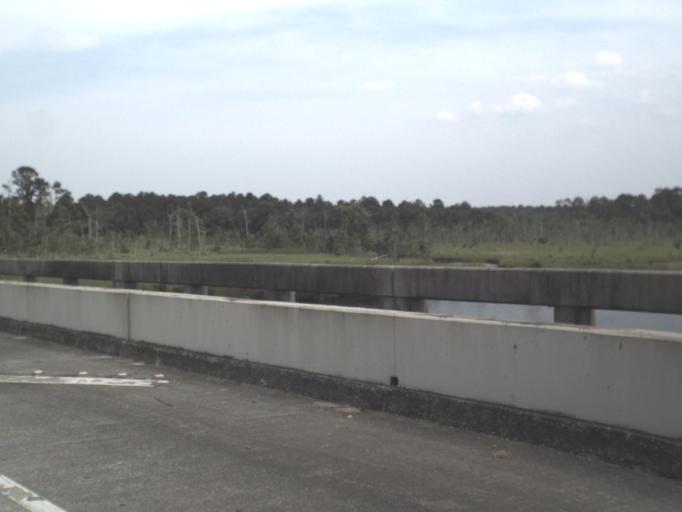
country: US
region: Florida
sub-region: Clay County
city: Bellair-Meadowbrook Terrace
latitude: 30.2474
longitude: -81.7095
